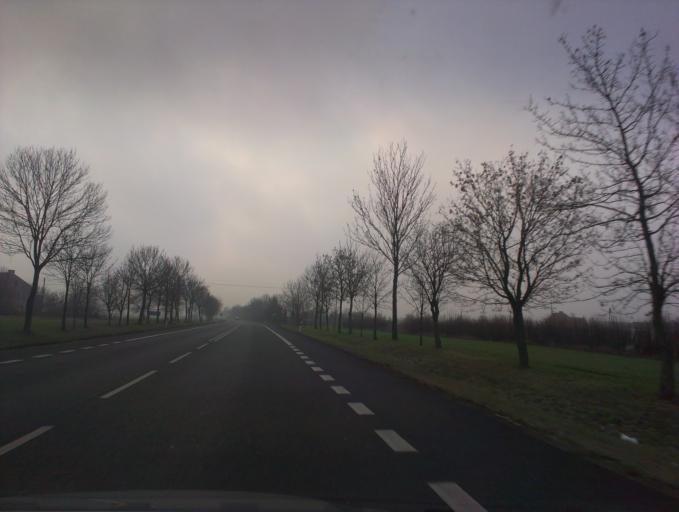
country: PL
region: Greater Poland Voivodeship
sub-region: Powiat chodzieski
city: Budzyn
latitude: 52.8851
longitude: 16.9703
